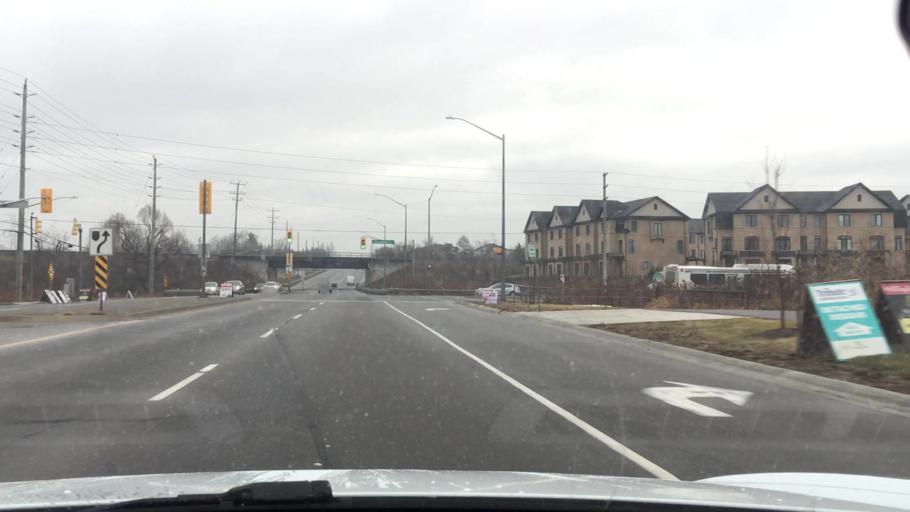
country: CA
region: Ontario
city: Ajax
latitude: 43.8948
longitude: -79.0421
